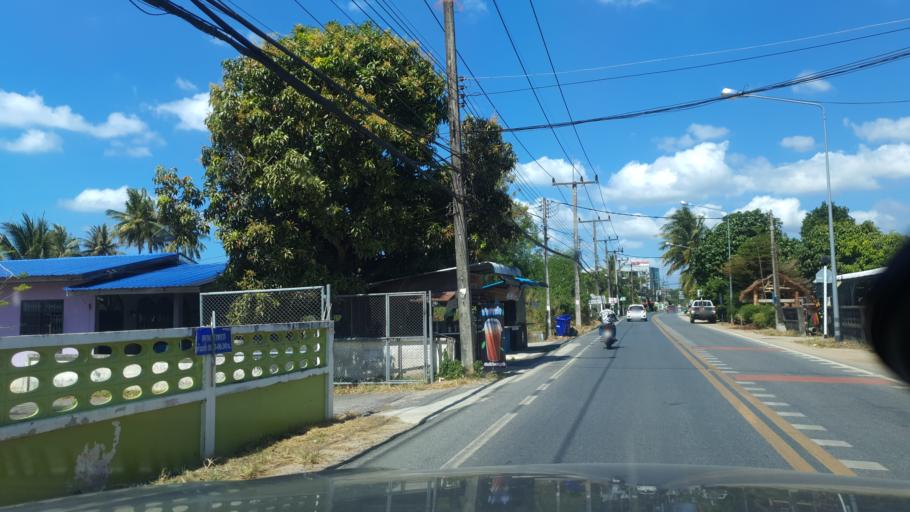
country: TH
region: Phuket
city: Thalang
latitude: 8.1322
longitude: 98.3075
